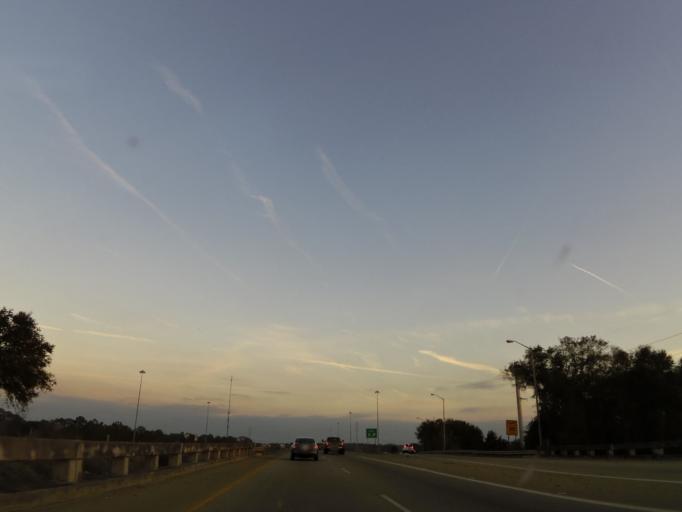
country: US
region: Georgia
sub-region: Dougherty County
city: Albany
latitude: 31.6082
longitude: -84.1572
